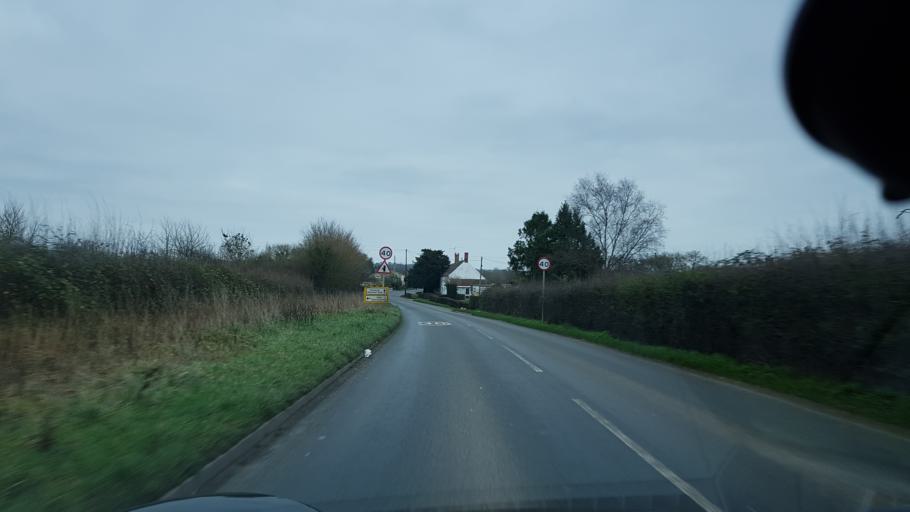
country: GB
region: England
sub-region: Somerset
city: Ilminster
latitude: 50.9487
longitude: -2.9315
